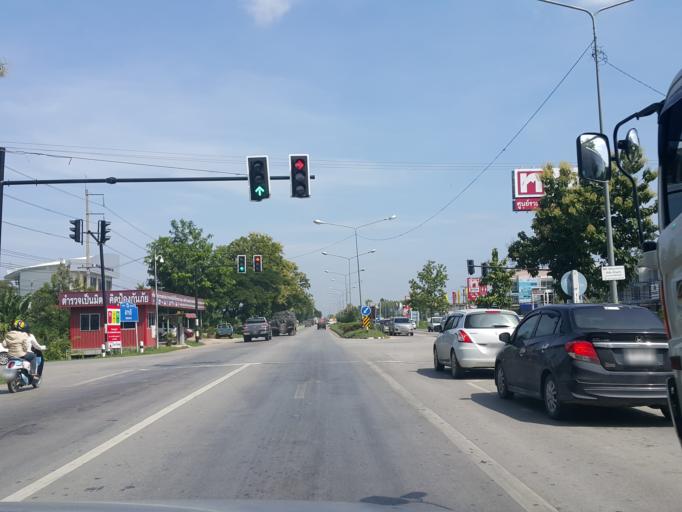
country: TH
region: Chiang Mai
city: Saraphi
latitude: 18.7182
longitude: 99.0427
